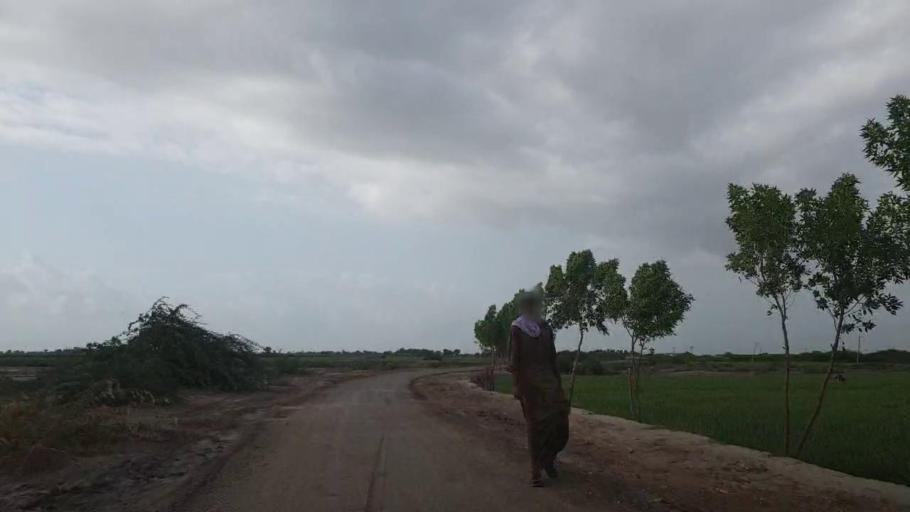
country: PK
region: Sindh
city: Kadhan
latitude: 24.5924
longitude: 69.0555
